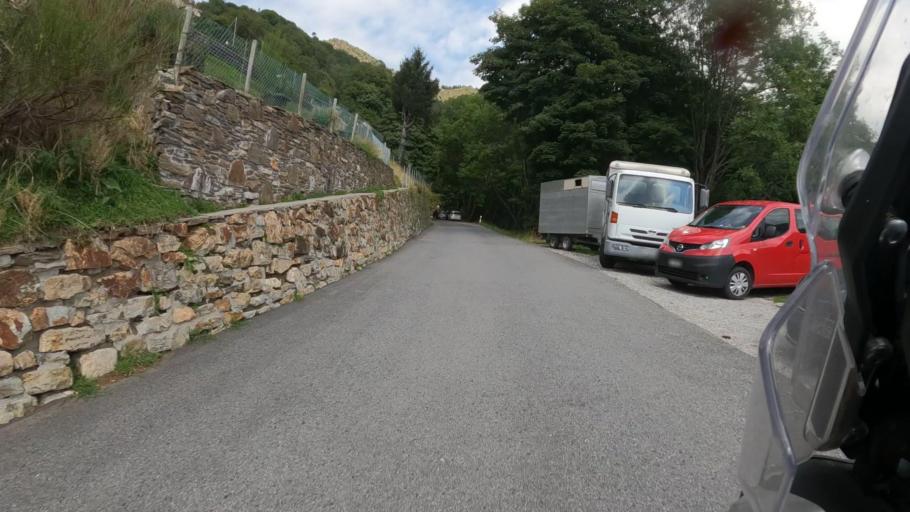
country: CH
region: Ticino
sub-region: Locarno District
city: Magadino
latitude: 46.1023
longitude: 8.8428
